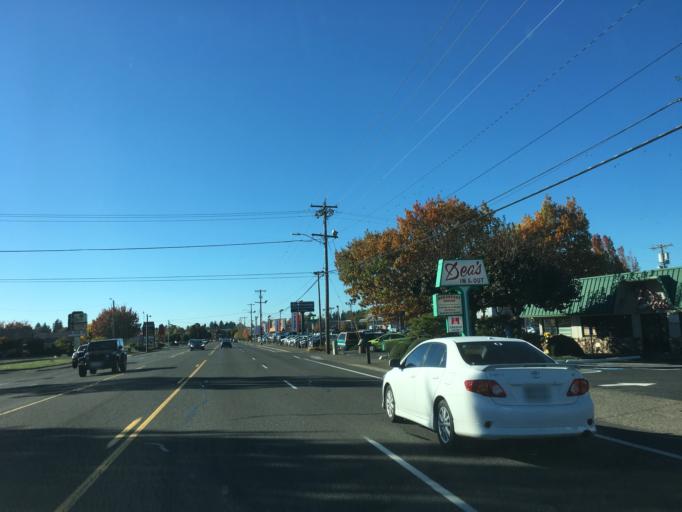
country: US
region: Oregon
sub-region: Multnomah County
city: Gresham
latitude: 45.5071
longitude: -122.4229
